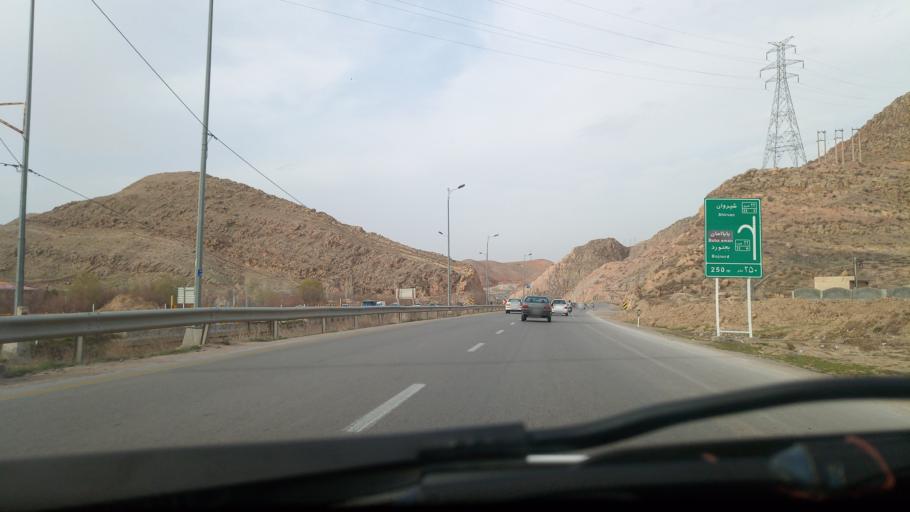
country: IR
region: Khorasan-e Shomali
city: Bojnurd
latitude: 37.4880
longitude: 57.4388
